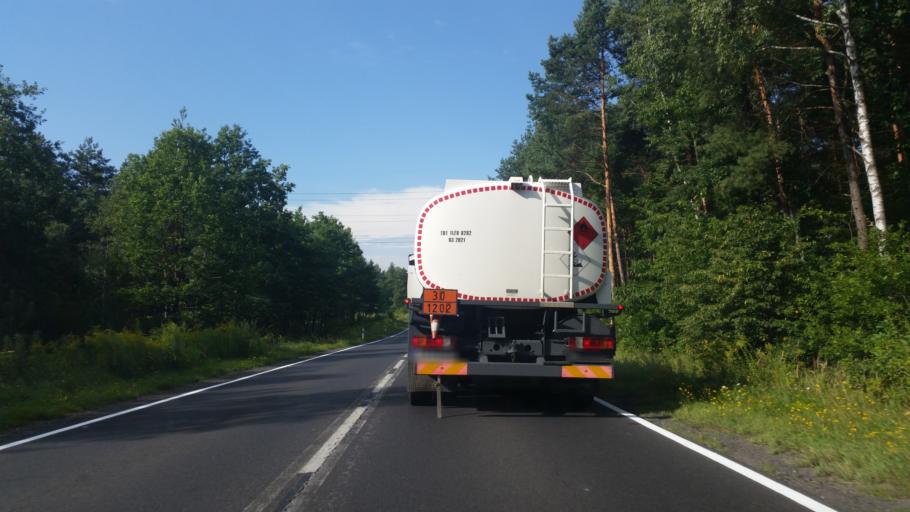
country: PL
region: Lesser Poland Voivodeship
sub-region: Powiat chrzanowski
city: Zarki
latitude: 50.1194
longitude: 19.3602
